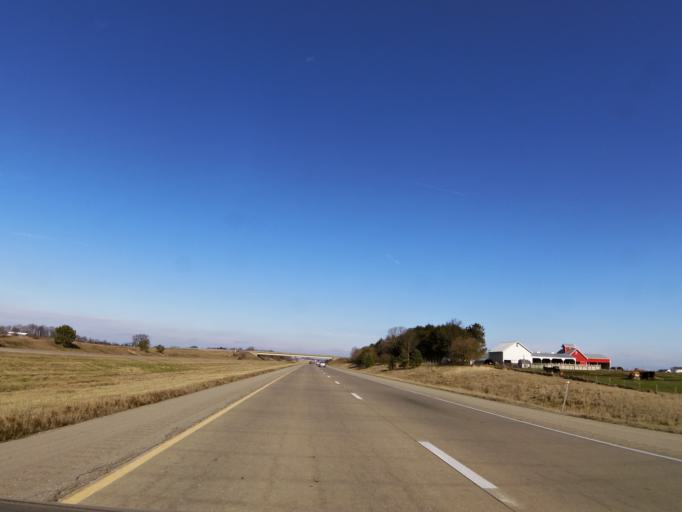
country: US
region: Illinois
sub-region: LaSalle County
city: La Salle
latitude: 41.4079
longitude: -89.0589
